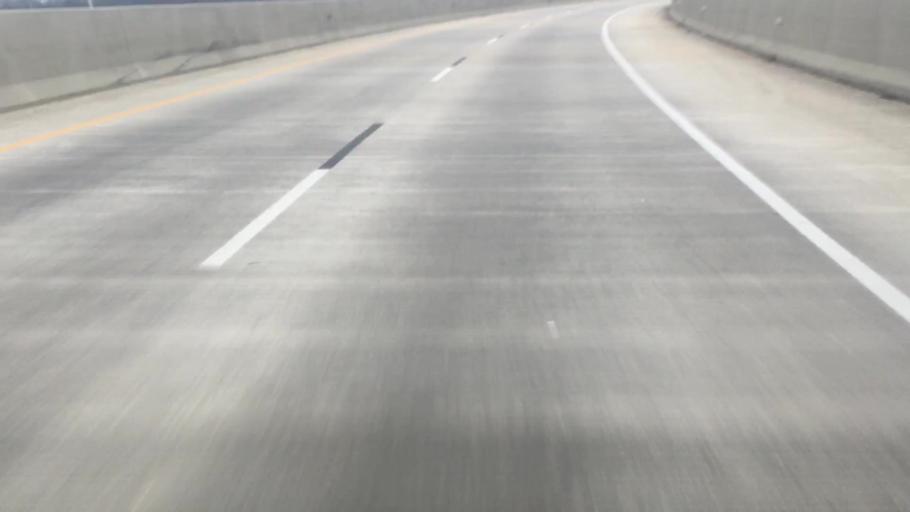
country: US
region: Alabama
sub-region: Jefferson County
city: Fultondale
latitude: 33.5737
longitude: -86.8192
